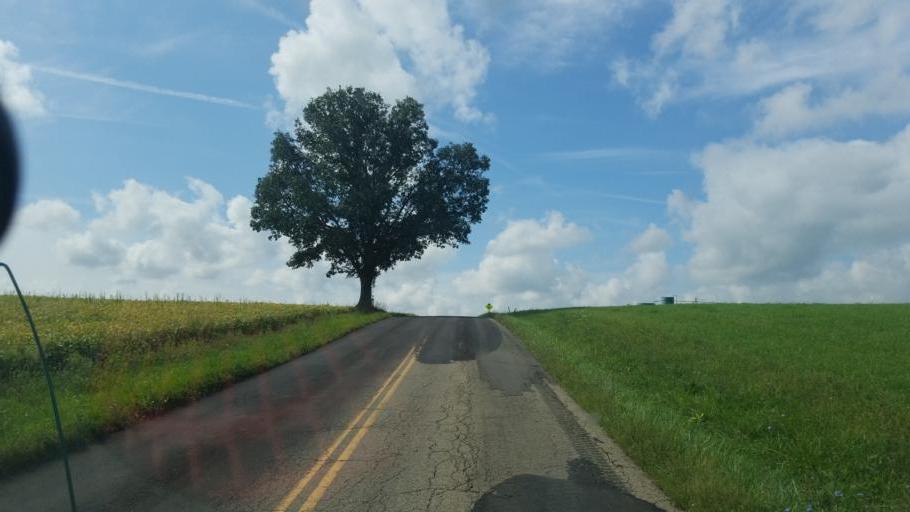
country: US
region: Ohio
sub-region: Knox County
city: Mount Vernon
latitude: 40.4821
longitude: -82.4352
